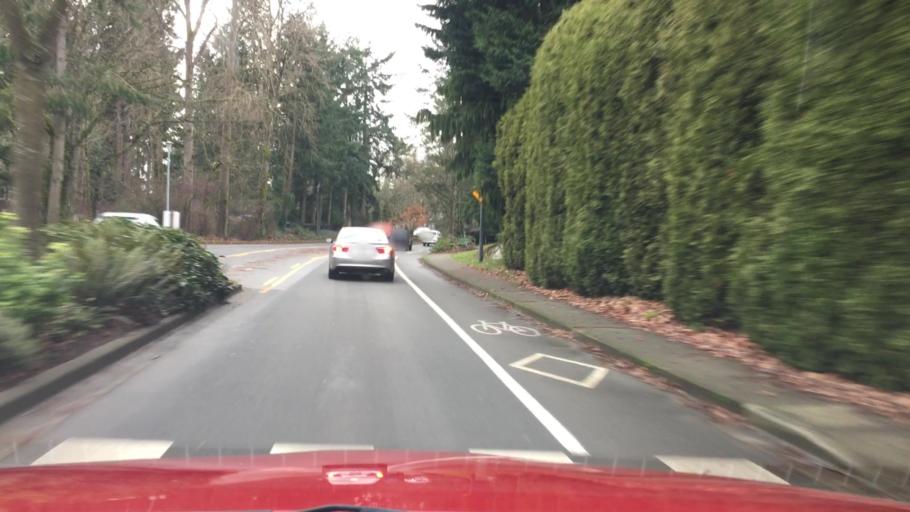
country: CA
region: British Columbia
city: Victoria
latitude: 48.4983
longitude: -123.3701
